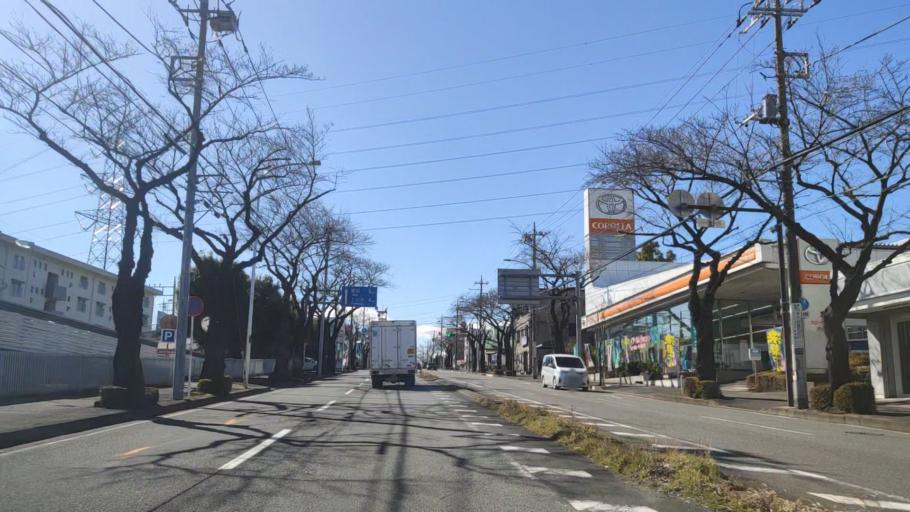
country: JP
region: Tokyo
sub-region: Machida-shi
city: Machida
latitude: 35.5151
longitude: 139.4993
